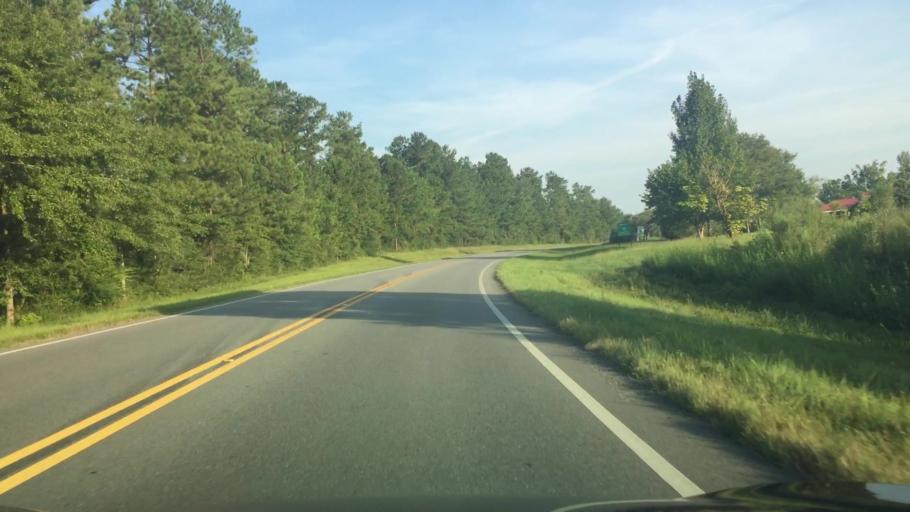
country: US
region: Alabama
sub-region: Covington County
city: Florala
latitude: 31.0130
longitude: -86.3581
